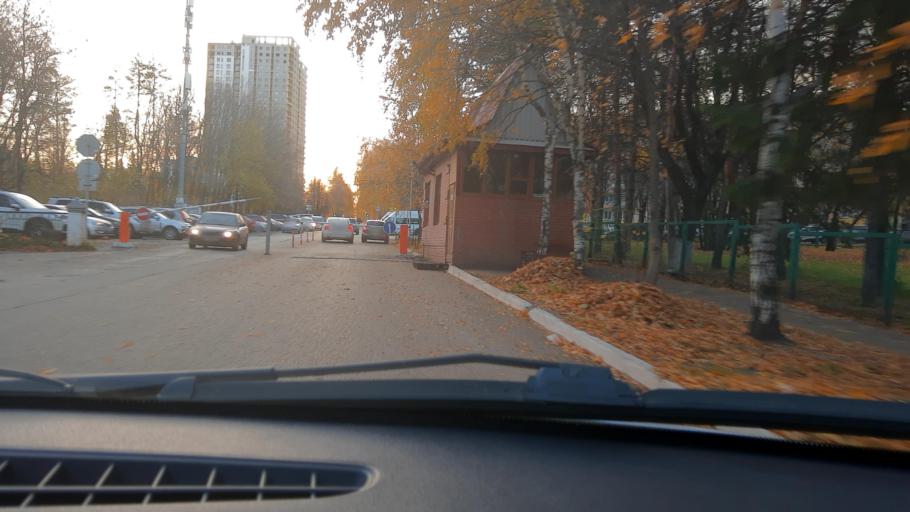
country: RU
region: Bashkortostan
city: Ufa
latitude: 54.7664
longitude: 55.9945
